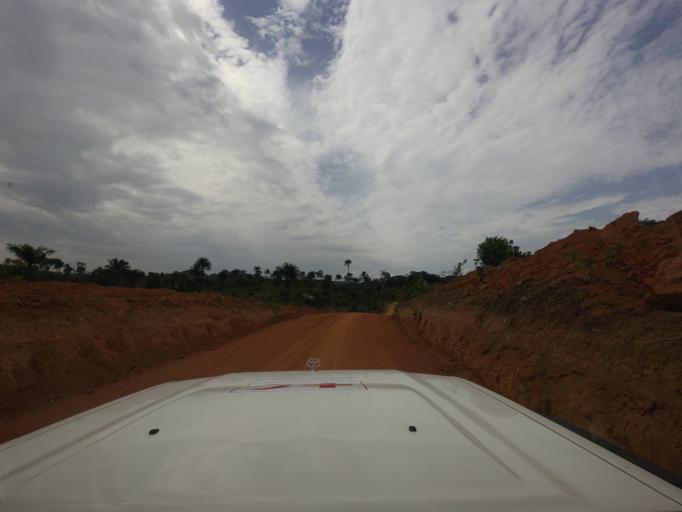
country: SL
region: Eastern Province
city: Buedu
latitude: 8.2487
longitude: -10.2236
